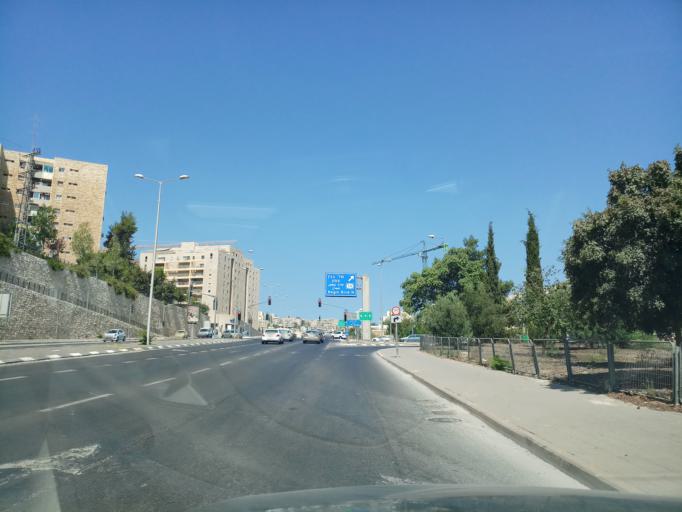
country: IL
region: Jerusalem
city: Jerusalem
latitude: 31.7665
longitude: 35.1965
